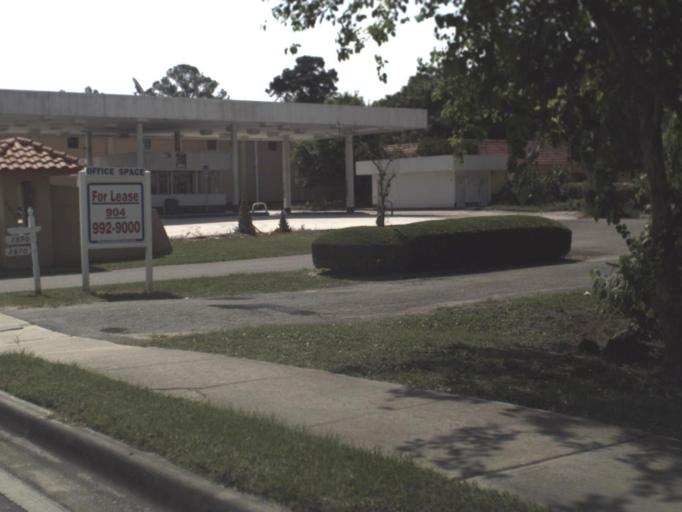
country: US
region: Florida
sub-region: Duval County
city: Jacksonville
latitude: 30.2609
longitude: -81.6289
